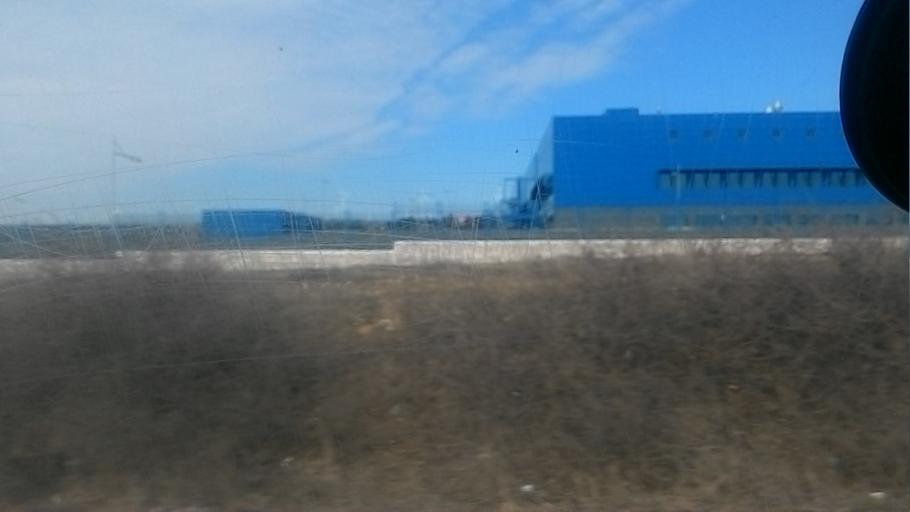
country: TR
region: Istanbul
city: Canta
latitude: 41.0821
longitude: 28.0486
